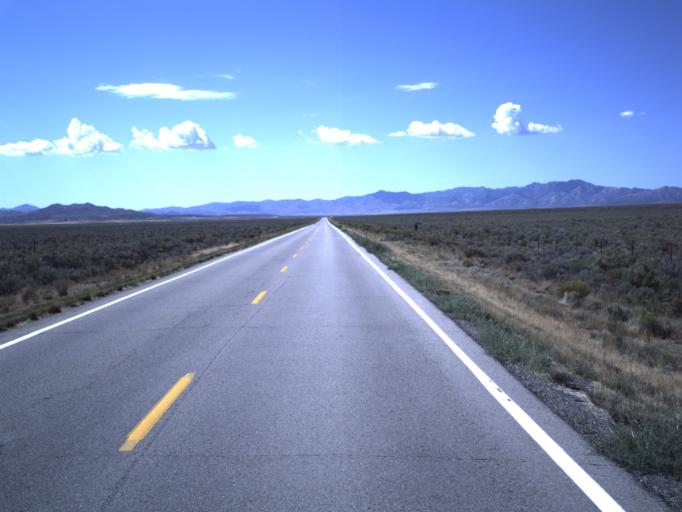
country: US
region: Utah
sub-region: Tooele County
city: Tooele
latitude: 40.2398
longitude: -112.4015
